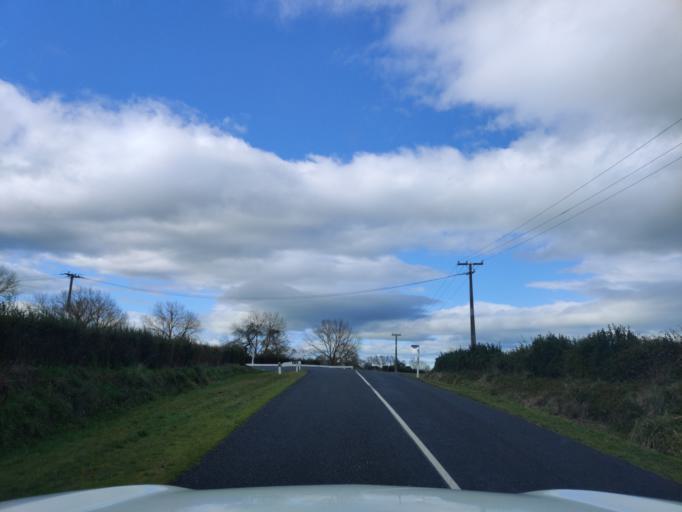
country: NZ
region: Waikato
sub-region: Hauraki District
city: Paeroa
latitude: -37.5942
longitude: 175.5222
